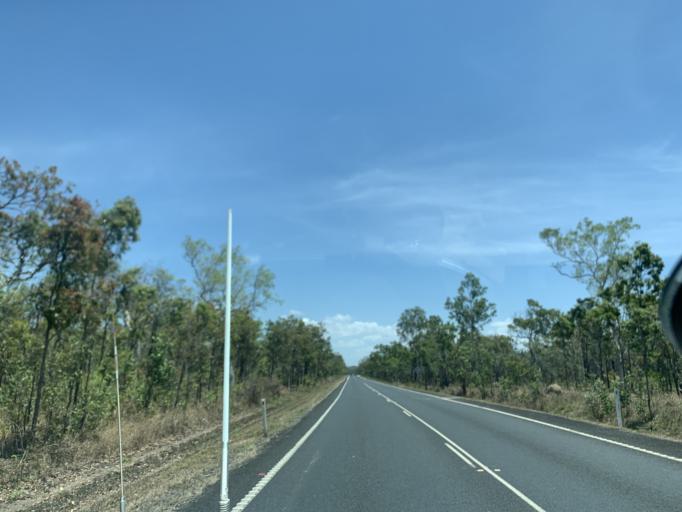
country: AU
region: Queensland
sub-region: Tablelands
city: Kuranda
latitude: -16.9217
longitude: 145.5518
